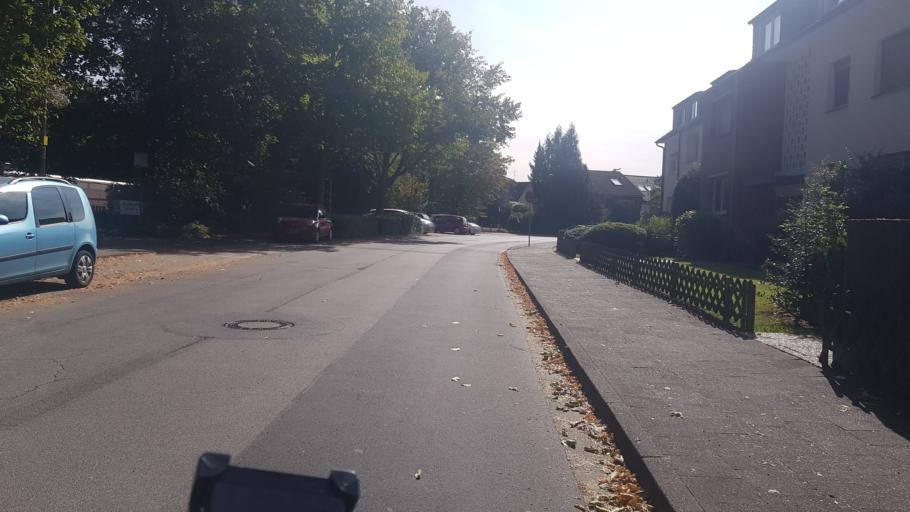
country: DE
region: North Rhine-Westphalia
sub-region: Regierungsbezirk Dusseldorf
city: Ratingen
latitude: 51.3431
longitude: 6.8266
